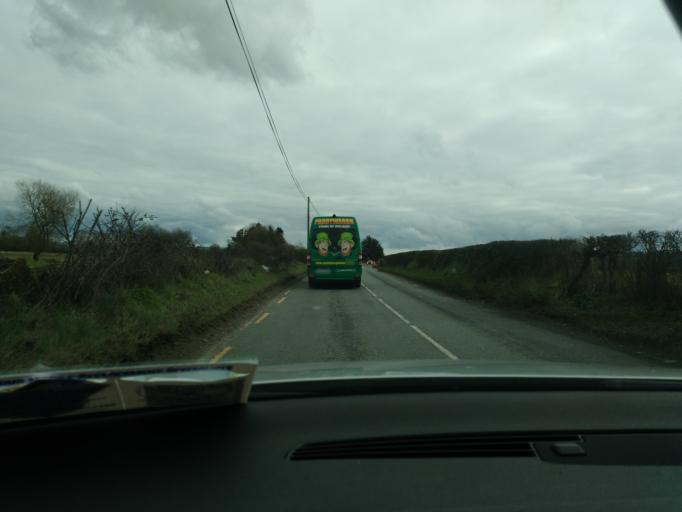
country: IE
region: Leinster
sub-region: Kilkenny
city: Ballyragget
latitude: 52.7297
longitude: -7.3839
